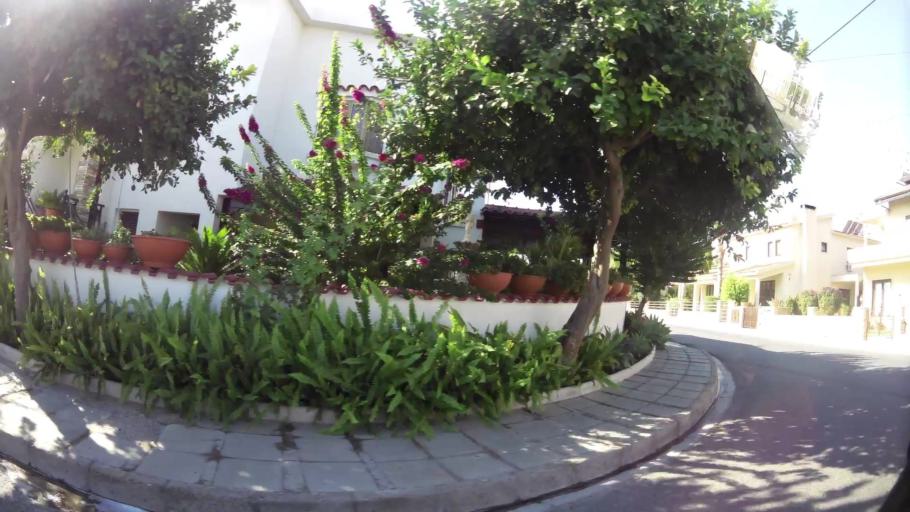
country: CY
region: Larnaka
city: Aradippou
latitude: 34.9462
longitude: 33.5876
